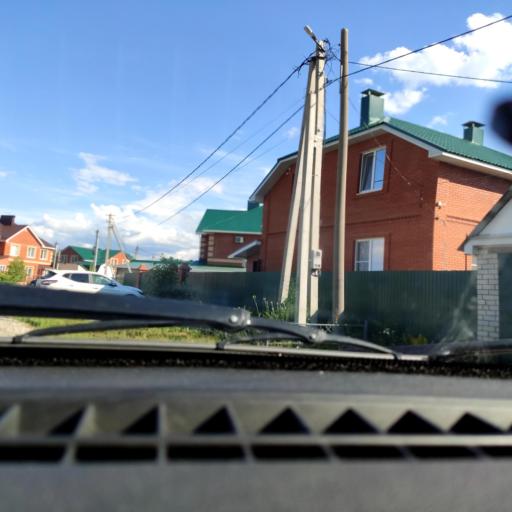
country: RU
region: Bashkortostan
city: Ufa
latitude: 54.6295
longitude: 55.9222
